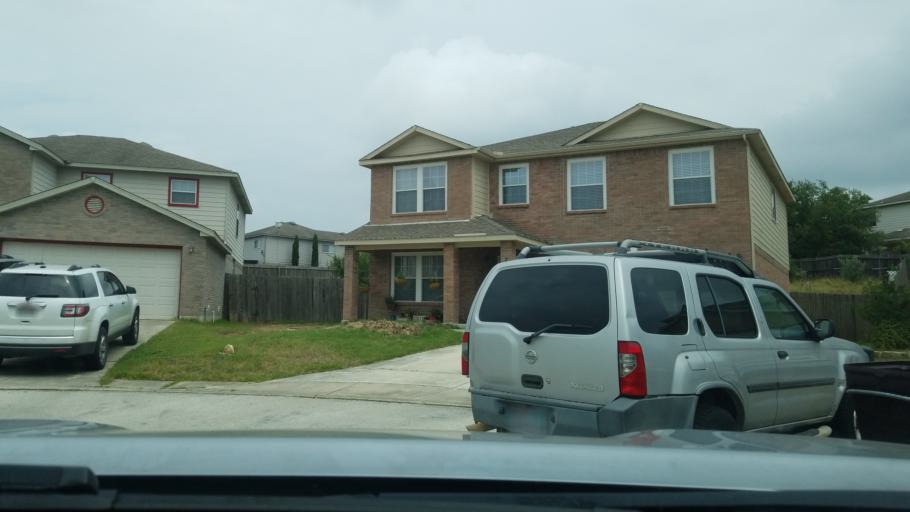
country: US
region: Texas
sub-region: Bexar County
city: Timberwood Park
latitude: 29.6815
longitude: -98.4630
